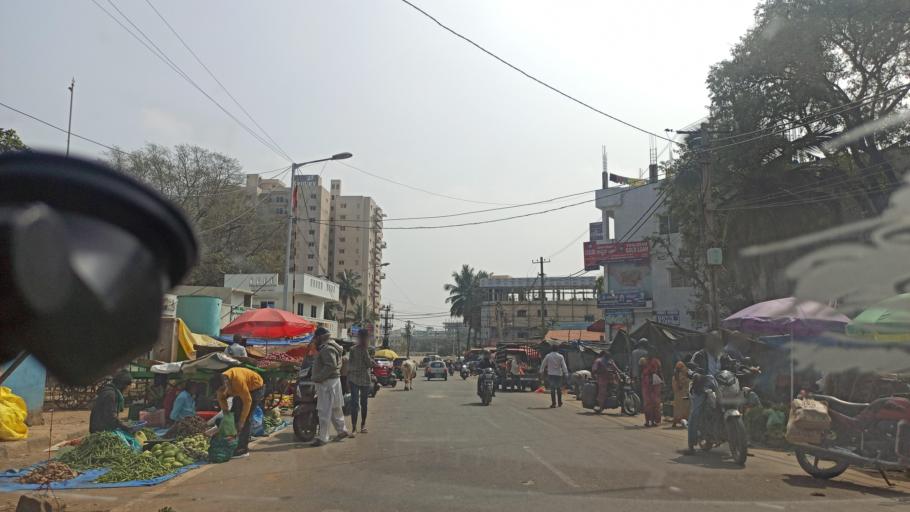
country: IN
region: Karnataka
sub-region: Bangalore Urban
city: Yelahanka
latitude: 13.0971
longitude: 77.5996
